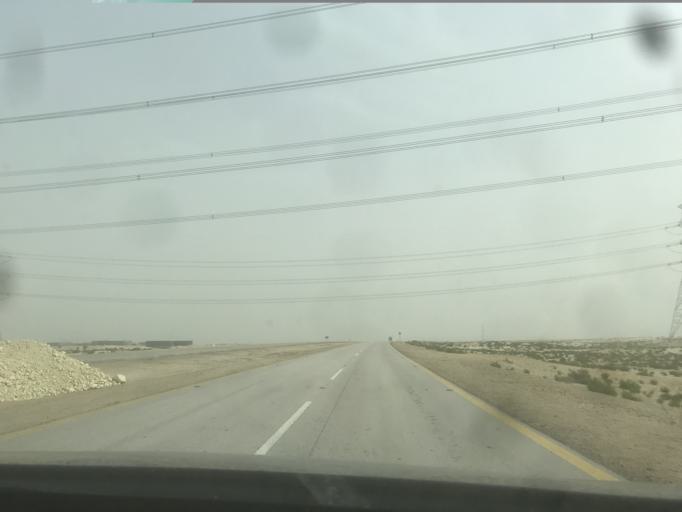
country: SA
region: Eastern Province
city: Abqaiq
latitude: 25.9107
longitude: 49.9587
